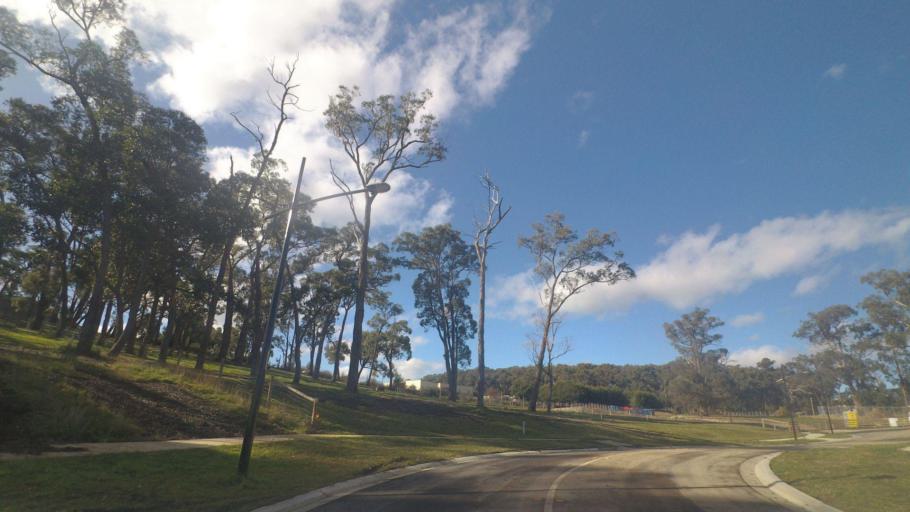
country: AU
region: Victoria
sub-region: Yarra Ranges
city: Lysterfield
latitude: -37.9198
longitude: 145.2917
